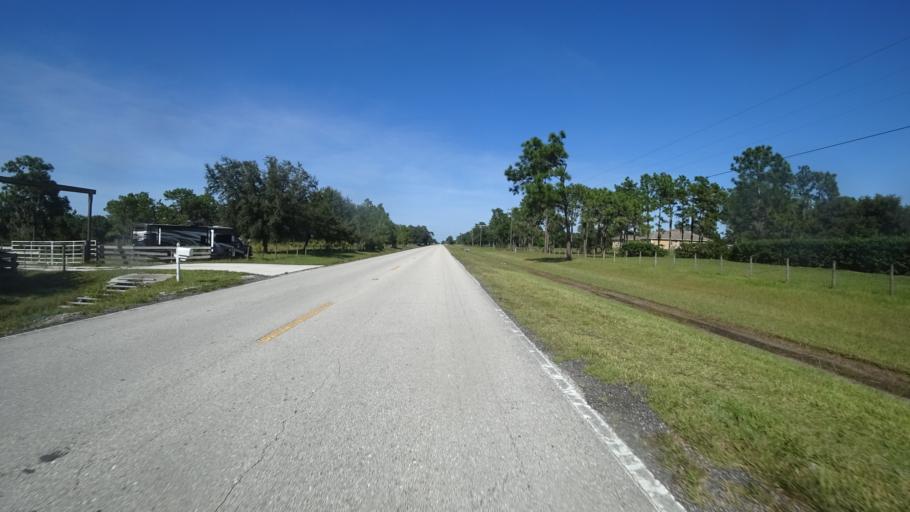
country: US
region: Florida
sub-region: Sarasota County
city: The Meadows
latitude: 27.4100
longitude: -82.3038
